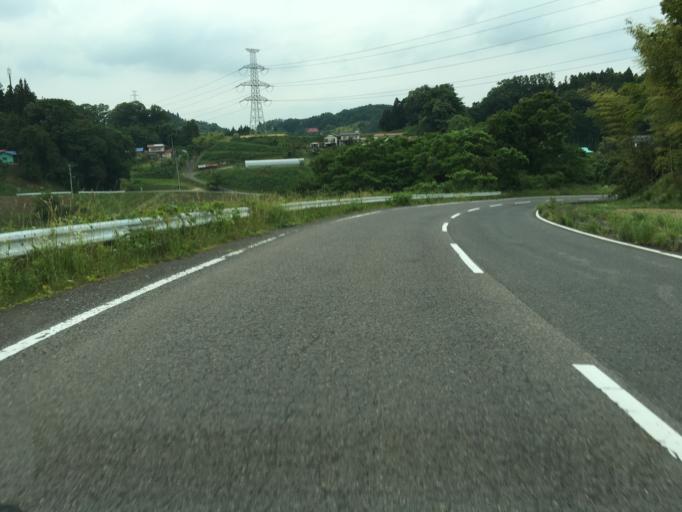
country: JP
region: Fukushima
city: Nihommatsu
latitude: 37.6086
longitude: 140.5597
